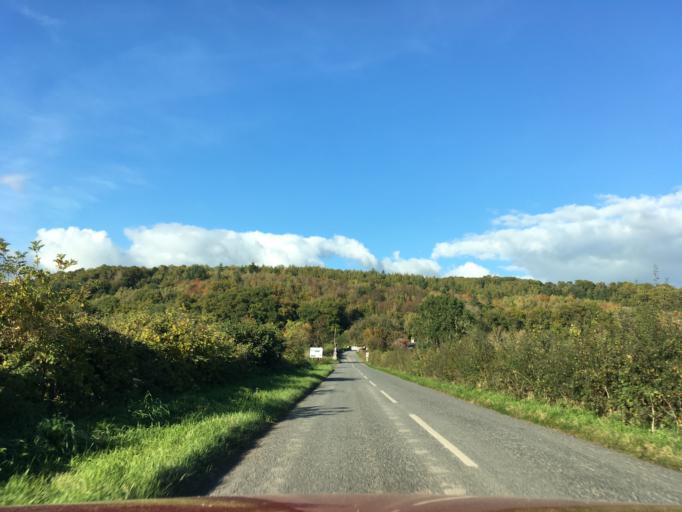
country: GB
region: England
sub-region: Herefordshire
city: Clifford
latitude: 52.1183
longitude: -3.0842
